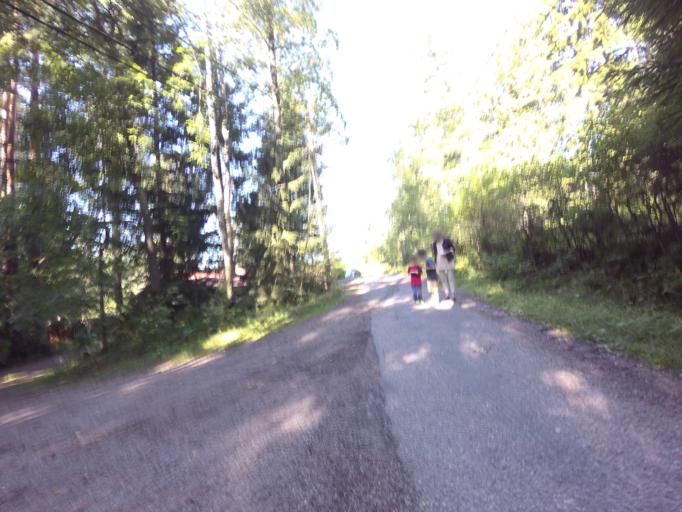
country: FI
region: Uusimaa
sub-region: Helsinki
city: Espoo
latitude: 60.1497
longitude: 24.6759
